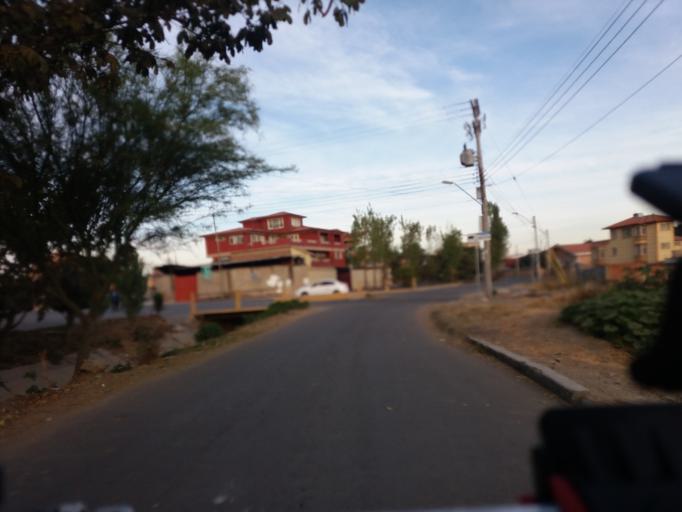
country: BO
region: Cochabamba
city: Cochabamba
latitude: -17.3607
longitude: -66.1886
